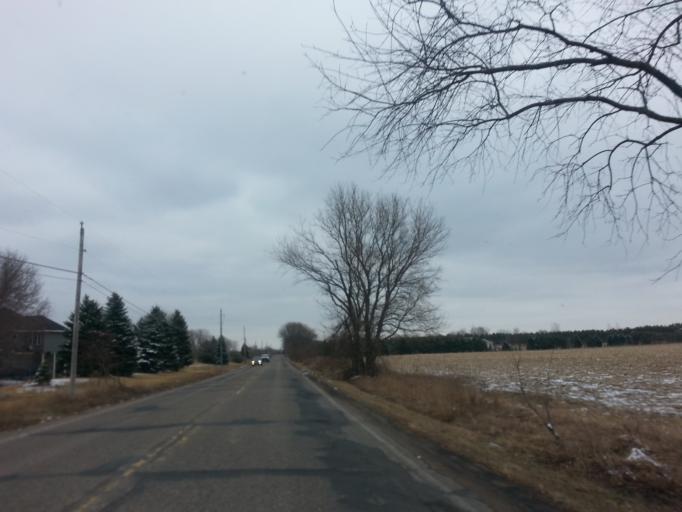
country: US
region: Wisconsin
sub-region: Saint Croix County
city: Hudson
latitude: 44.9802
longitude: -92.7905
